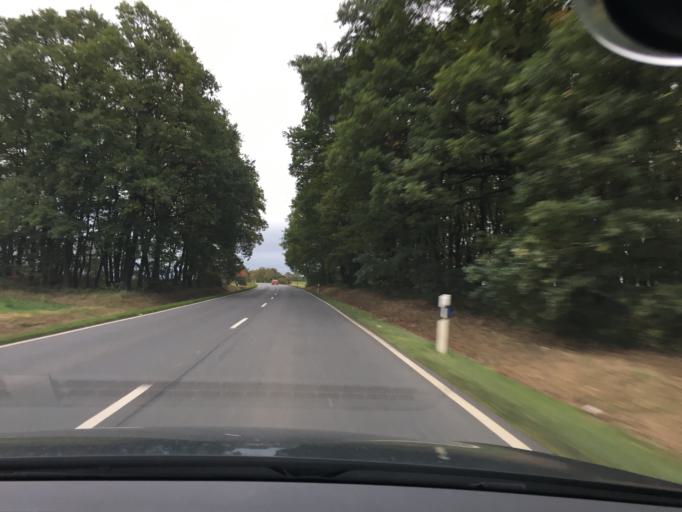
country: DE
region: North Rhine-Westphalia
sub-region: Regierungsbezirk Koln
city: Kreuzau
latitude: 50.7383
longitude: 6.5438
